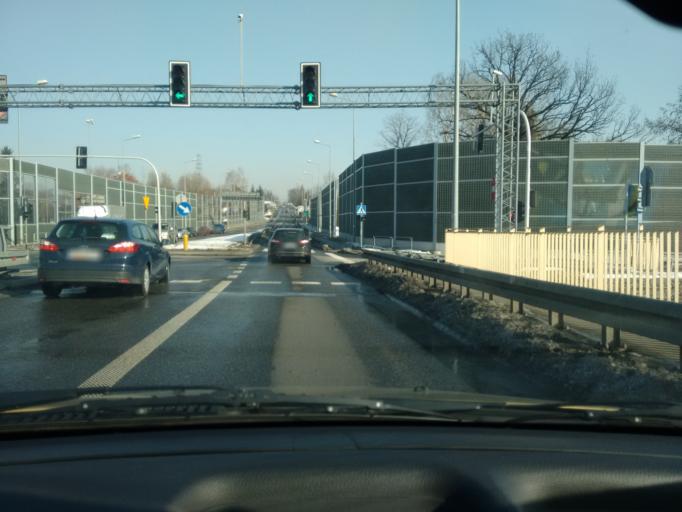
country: PL
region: Silesian Voivodeship
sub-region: Bielsko-Biala
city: Bielsko-Biala
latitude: 49.8236
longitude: 19.0867
